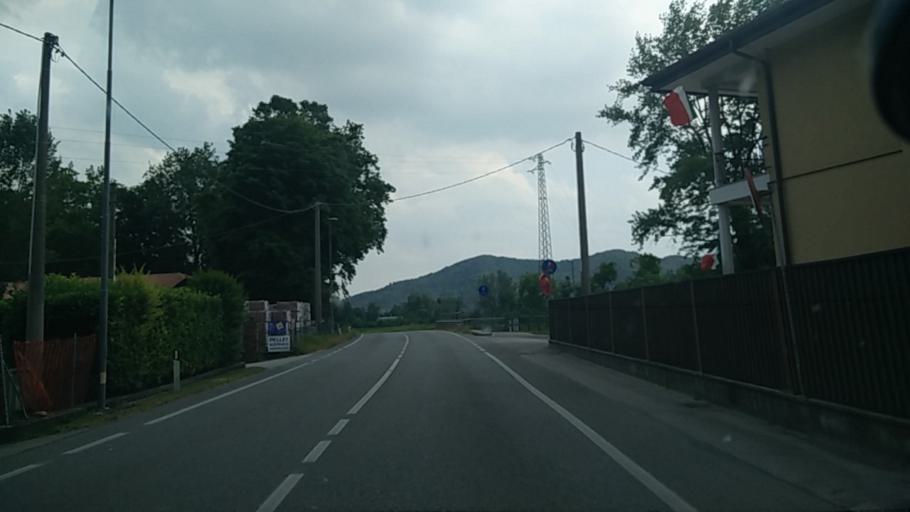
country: IT
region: Veneto
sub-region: Provincia di Treviso
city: Follina
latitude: 45.9466
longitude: 12.1237
